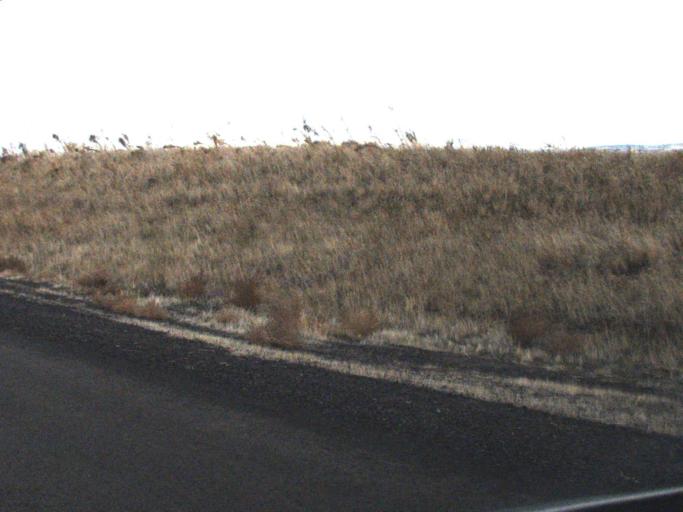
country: US
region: Washington
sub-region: Walla Walla County
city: Garrett
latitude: 46.0513
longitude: -118.5122
